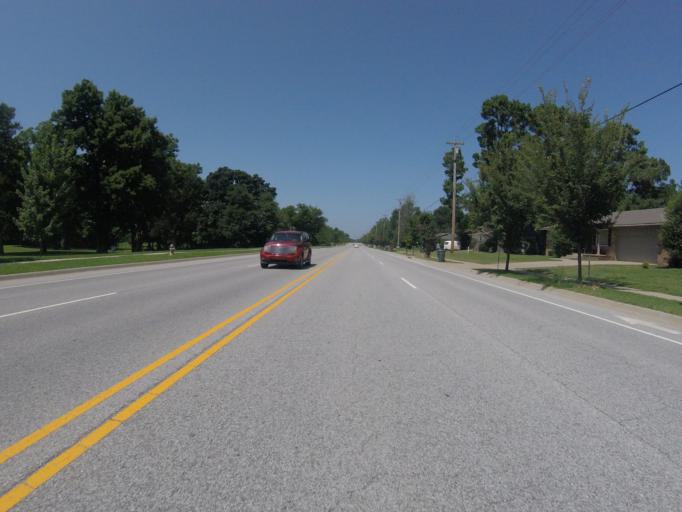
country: US
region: Arkansas
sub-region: Washington County
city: Fayetteville
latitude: 36.0927
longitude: -94.1986
